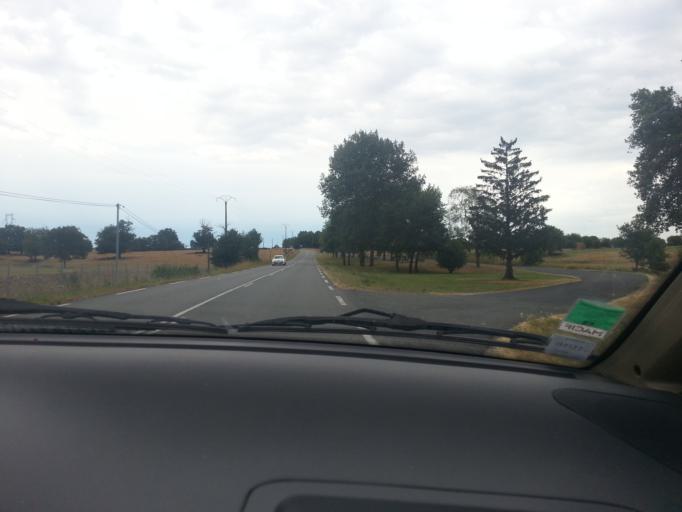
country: FR
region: Auvergne
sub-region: Departement de l'Allier
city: Saint-Gerand-le-Puy
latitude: 46.2099
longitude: 3.5087
